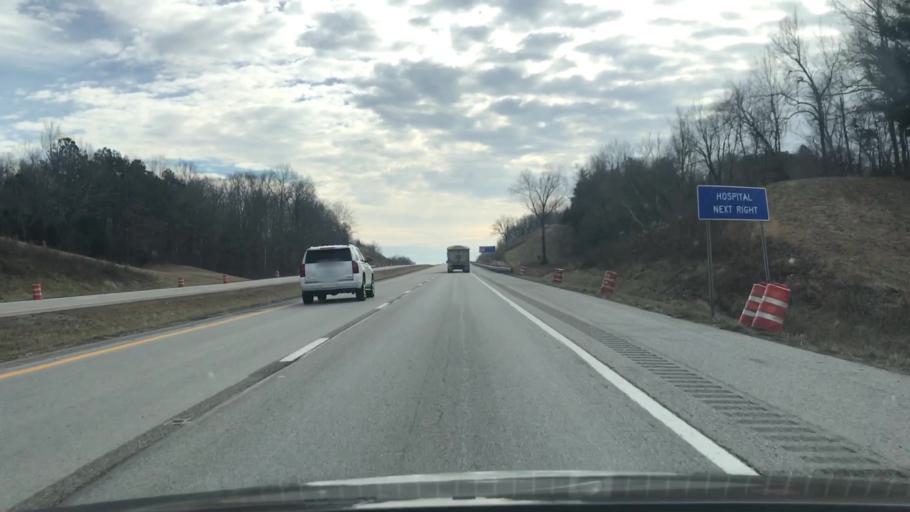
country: US
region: Kentucky
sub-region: Ohio County
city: Hartford
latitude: 37.4742
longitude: -86.8986
